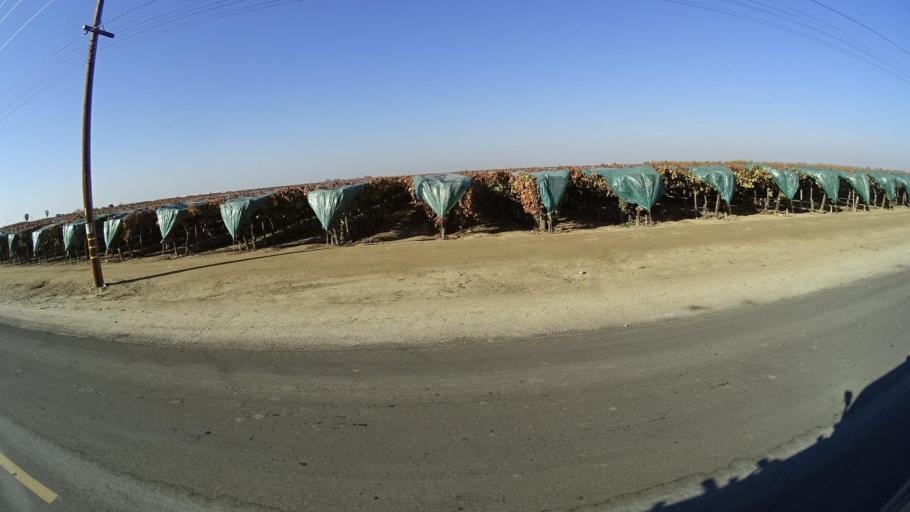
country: US
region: California
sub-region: Tulare County
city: Richgrove
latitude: 35.7530
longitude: -119.1341
